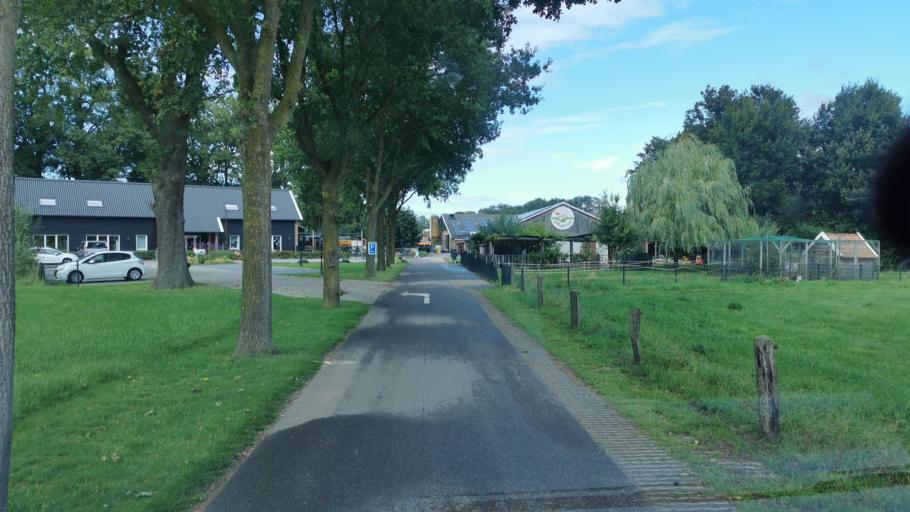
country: NL
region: Overijssel
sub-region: Gemeente Losser
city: Losser
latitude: 52.2700
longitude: 6.9795
